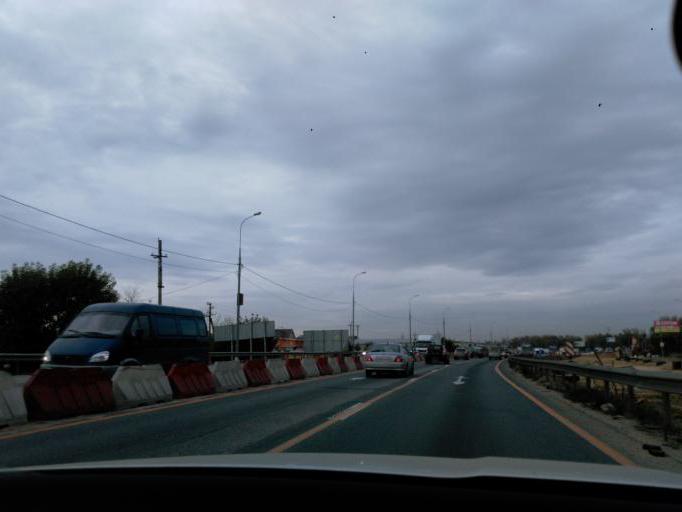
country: RU
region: Moscow
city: Severnyy
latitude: 55.9657
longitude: 37.5343
